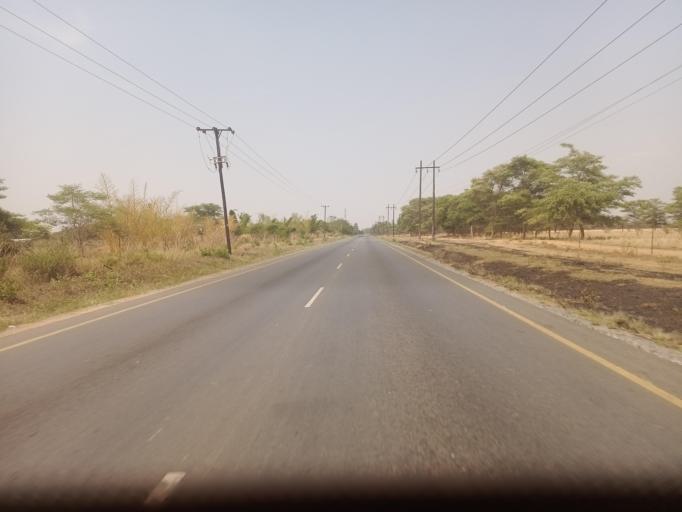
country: ZM
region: Lusaka
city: Lusaka
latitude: -15.2824
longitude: 28.3887
